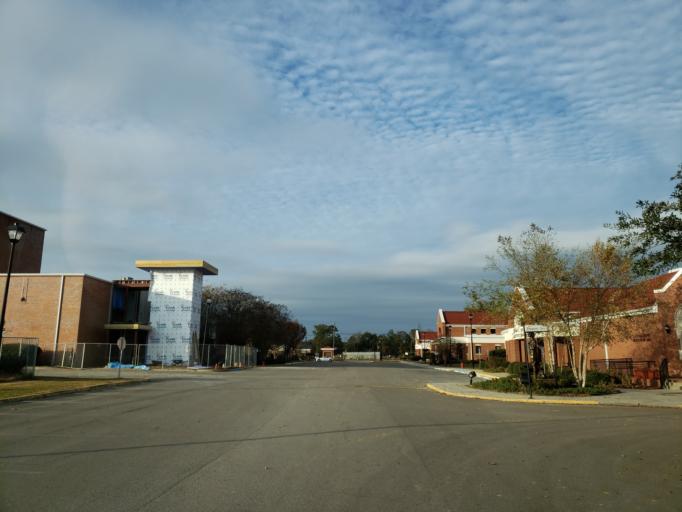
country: US
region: Mississippi
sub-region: Forrest County
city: Hattiesburg
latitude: 31.3047
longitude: -89.2905
